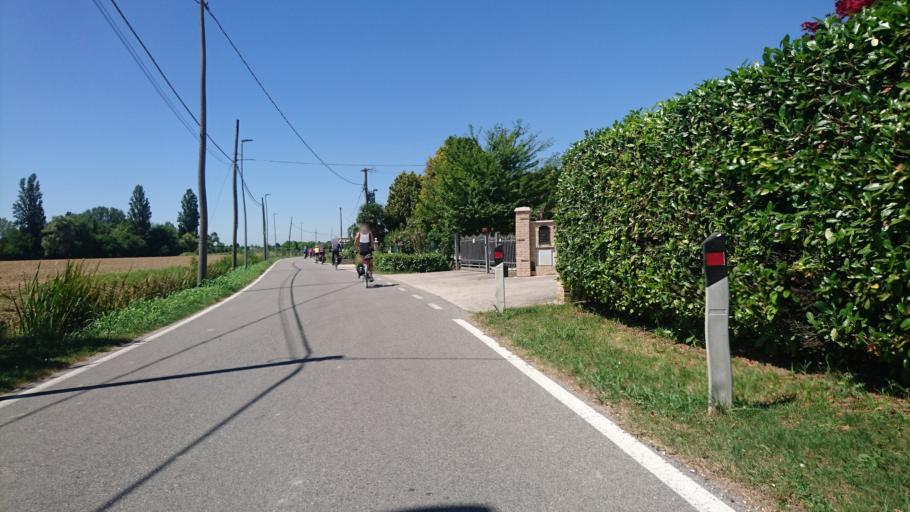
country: IT
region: Veneto
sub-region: Provincia di Padova
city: Bertipaglia
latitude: 45.3022
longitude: 11.8905
